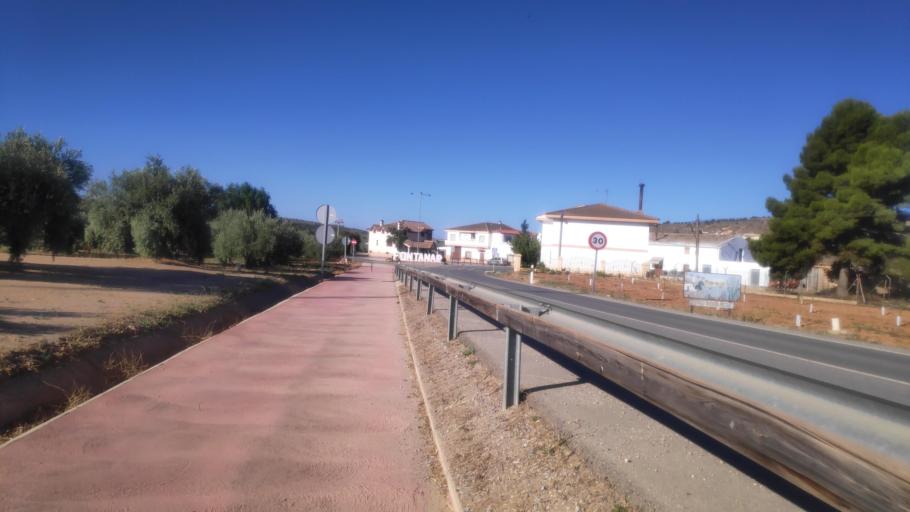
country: ES
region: Andalusia
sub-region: Provincia de Jaen
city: Pozo Alcon
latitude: 37.6723
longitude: -2.9670
